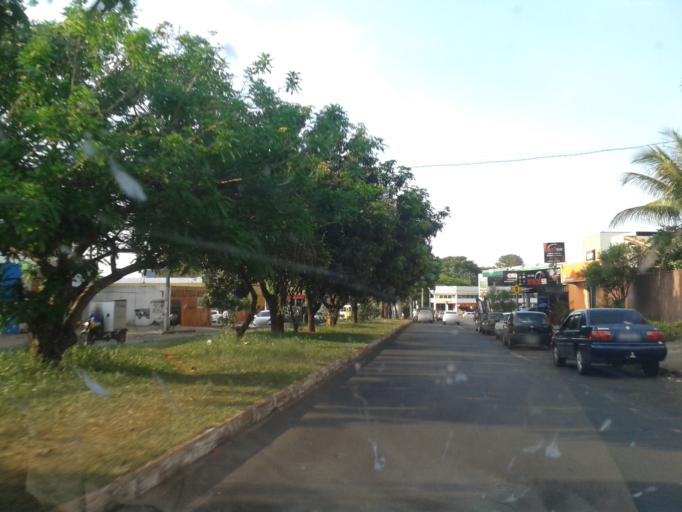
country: BR
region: Minas Gerais
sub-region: Uberlandia
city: Uberlandia
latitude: -18.9307
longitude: -48.3203
